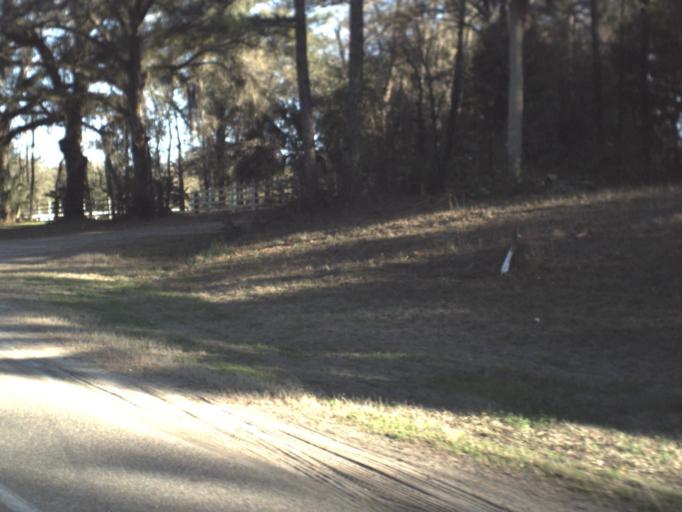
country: US
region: Florida
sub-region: Jefferson County
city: Monticello
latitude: 30.5204
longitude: -84.0540
